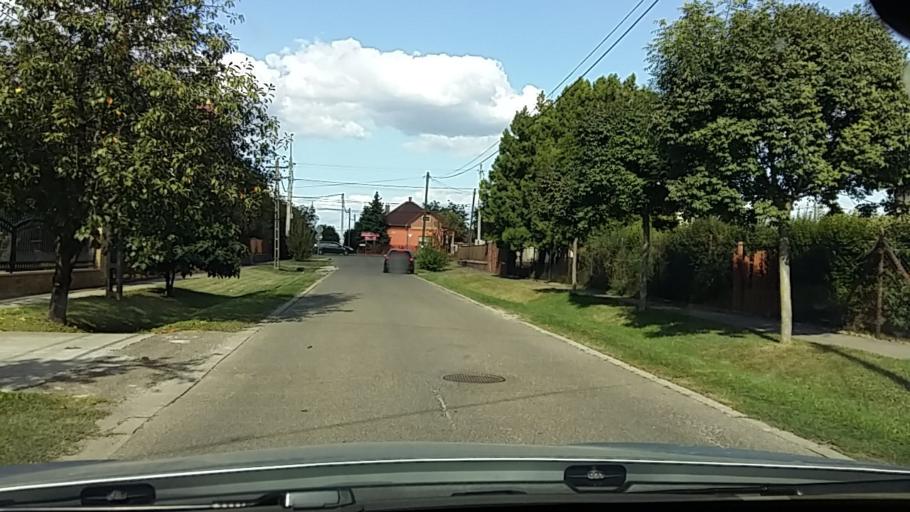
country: HU
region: Pest
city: Vecses
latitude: 47.4129
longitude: 19.2644
